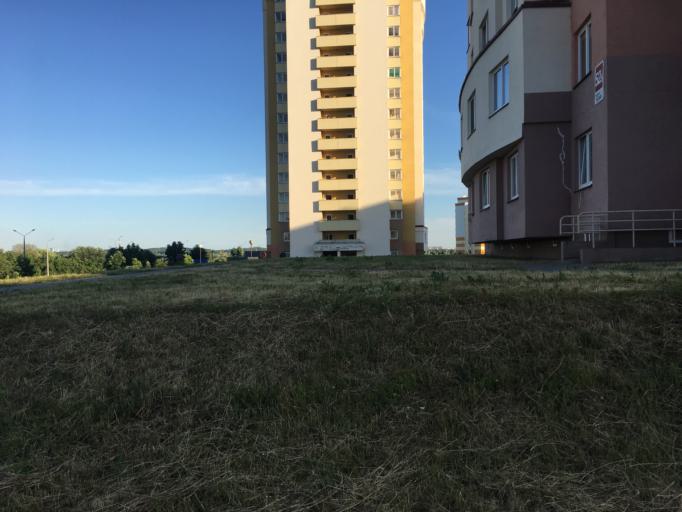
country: BY
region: Grodnenskaya
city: Hrodna
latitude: 53.7104
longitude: 23.8595
